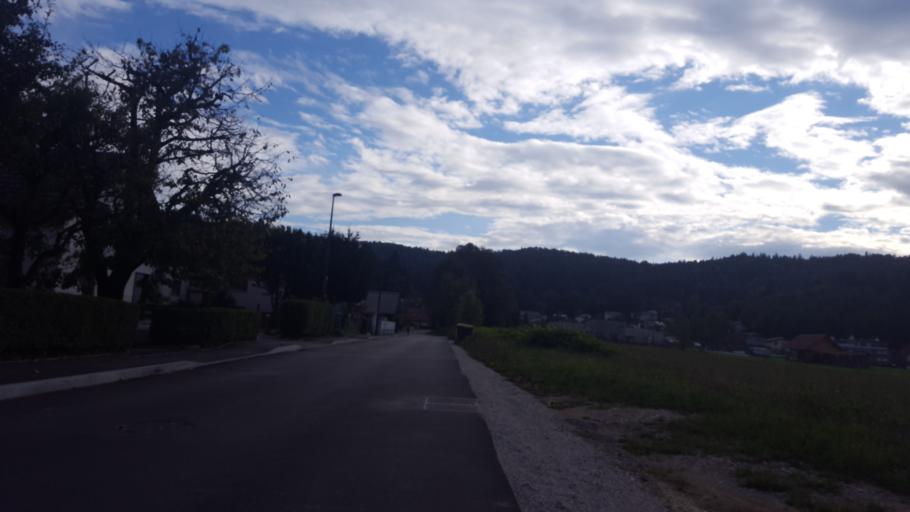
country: SI
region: Skofljica
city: Lavrica
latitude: 46.0436
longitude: 14.5582
